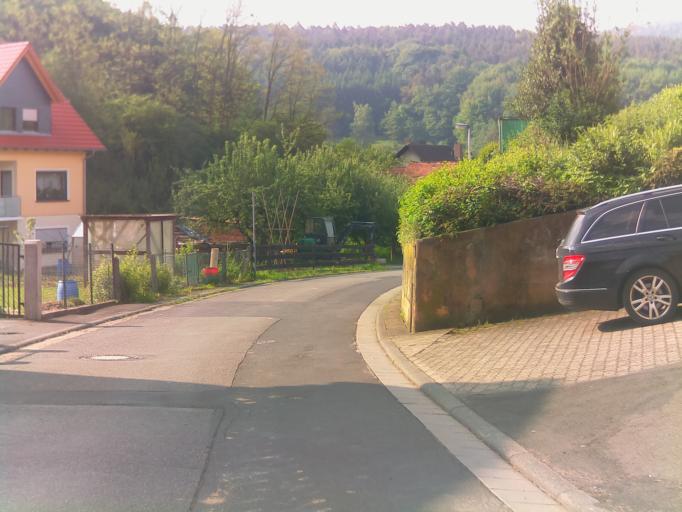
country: DE
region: Bavaria
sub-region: Regierungsbezirk Unterfranken
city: Heimbuchenthal
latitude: 49.8648
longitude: 9.3108
